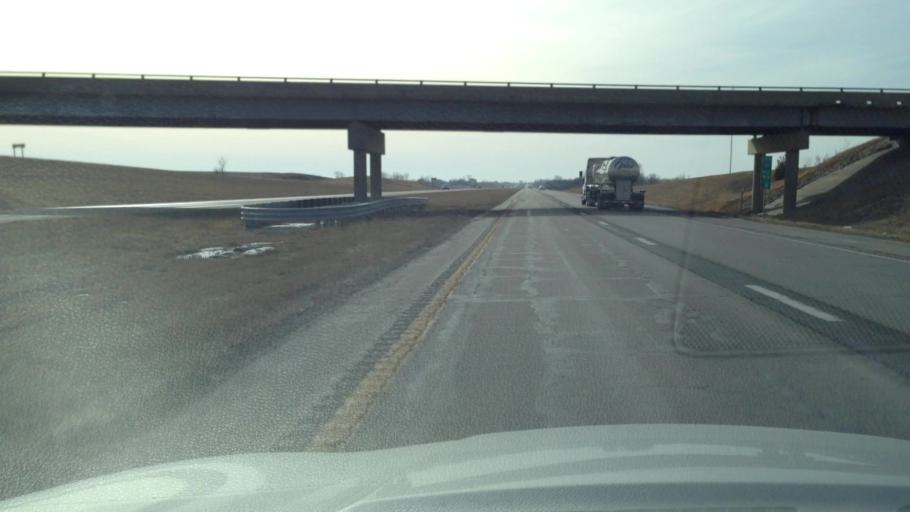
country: US
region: Missouri
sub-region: Harrison County
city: Bethany
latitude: 40.3749
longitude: -94.0030
